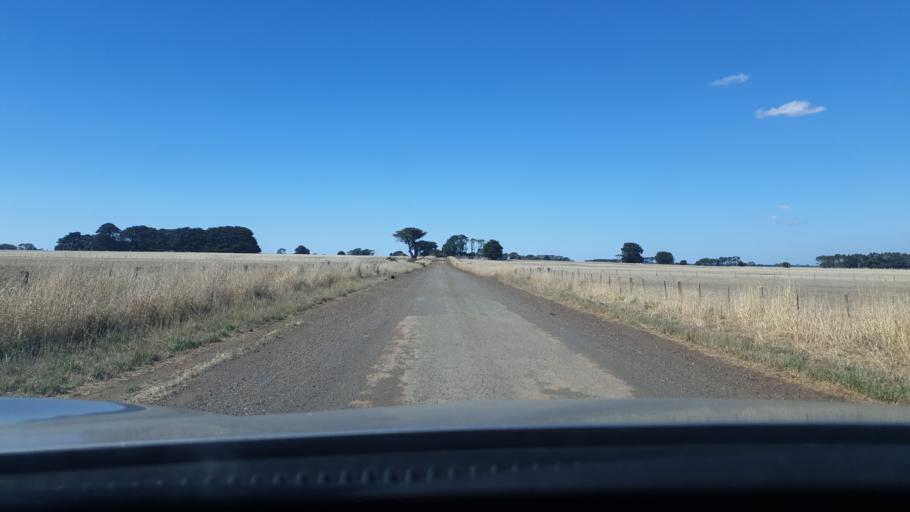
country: AU
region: Victoria
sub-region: Warrnambool
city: Warrnambool
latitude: -38.1649
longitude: 142.3799
